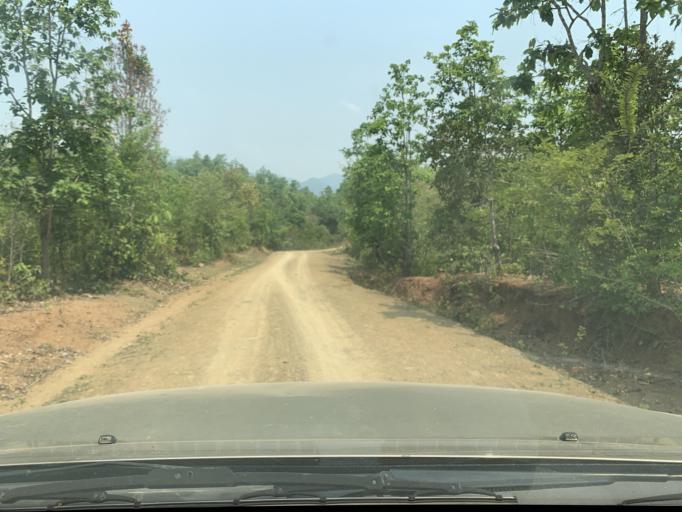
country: LA
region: Louangphabang
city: Louangphabang
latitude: 19.9395
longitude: 102.1330
